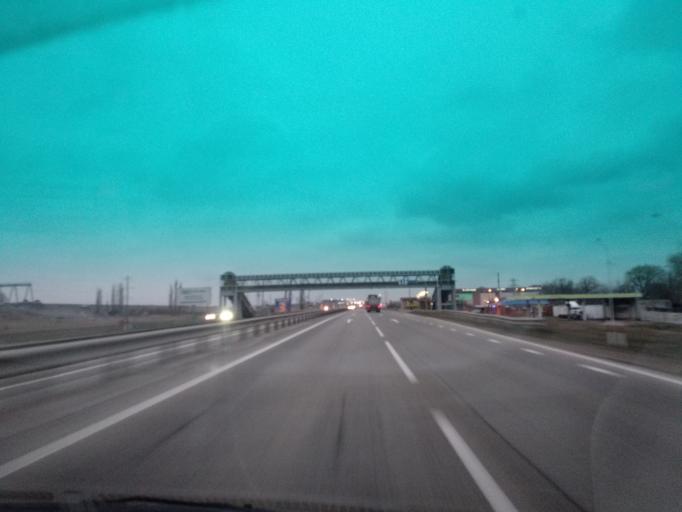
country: RU
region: Adygeya
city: Adygeysk
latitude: 44.9140
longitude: 39.1506
